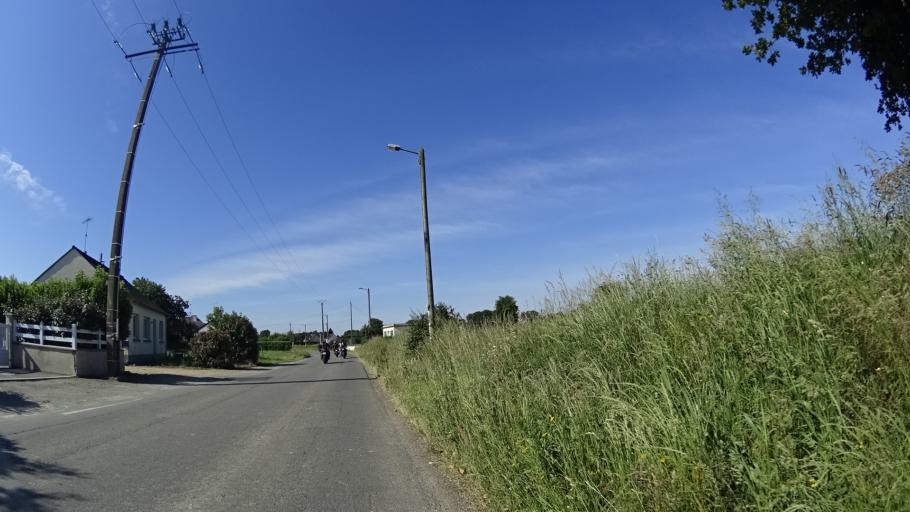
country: FR
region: Brittany
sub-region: Departement d'Ille-et-Vilaine
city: Guipry
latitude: 47.8182
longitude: -1.8475
